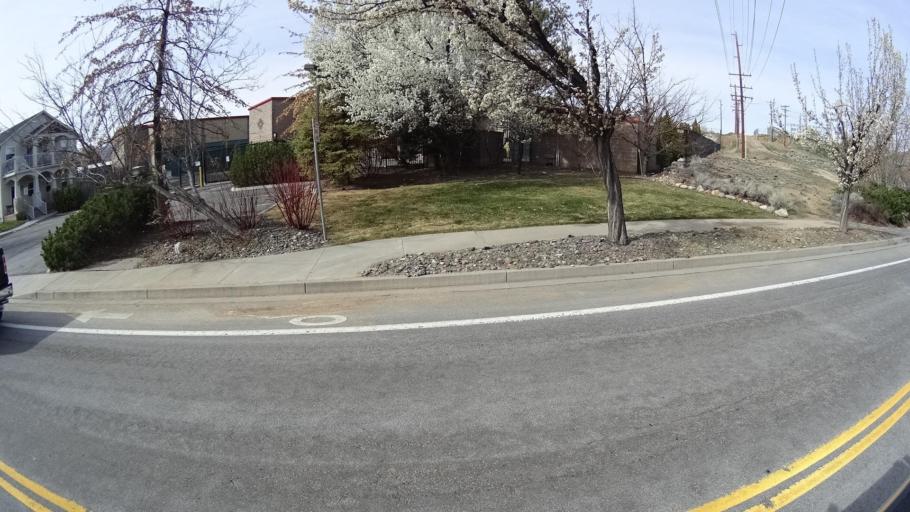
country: US
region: Nevada
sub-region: Washoe County
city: Reno
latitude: 39.5411
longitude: -119.8637
